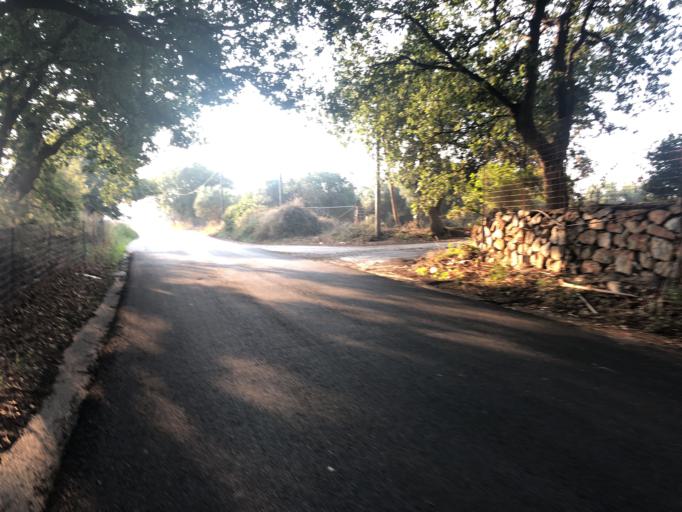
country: GR
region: Crete
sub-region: Nomos Chanias
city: Georgioupolis
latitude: 35.3497
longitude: 24.2809
